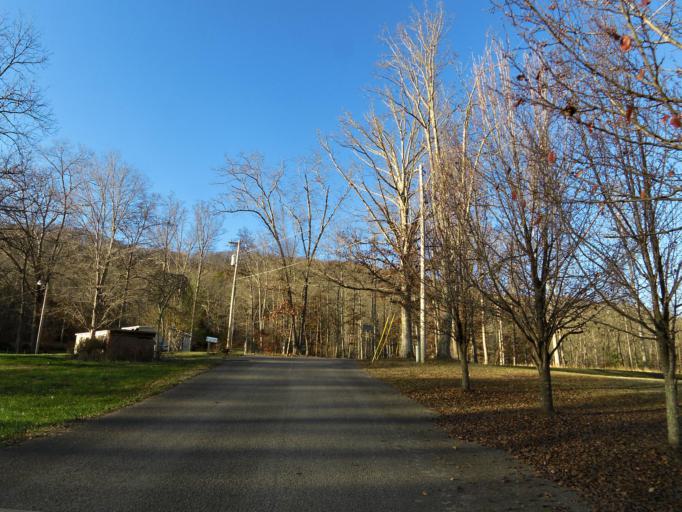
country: US
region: Tennessee
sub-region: Anderson County
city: Oak Ridge
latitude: 36.0915
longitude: -84.2397
